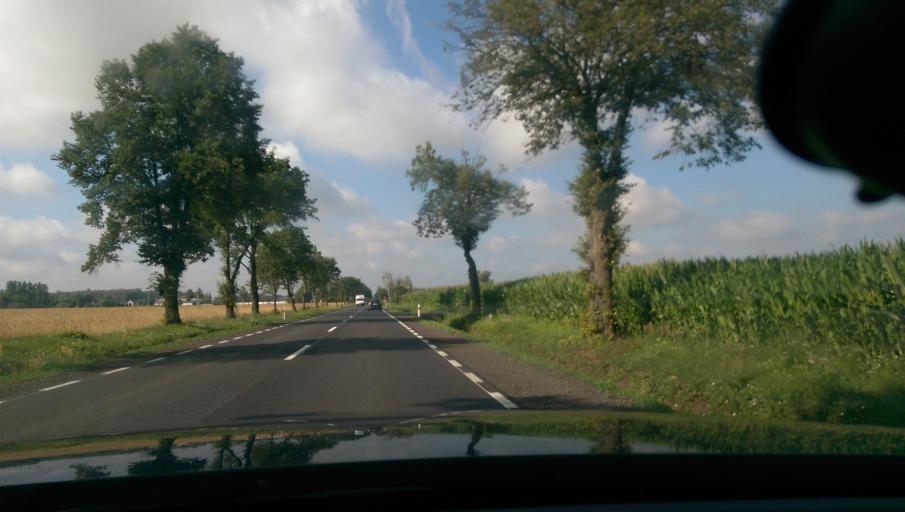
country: PL
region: Masovian Voivodeship
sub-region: Powiat ciechanowski
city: Ojrzen
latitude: 52.7368
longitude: 20.5199
